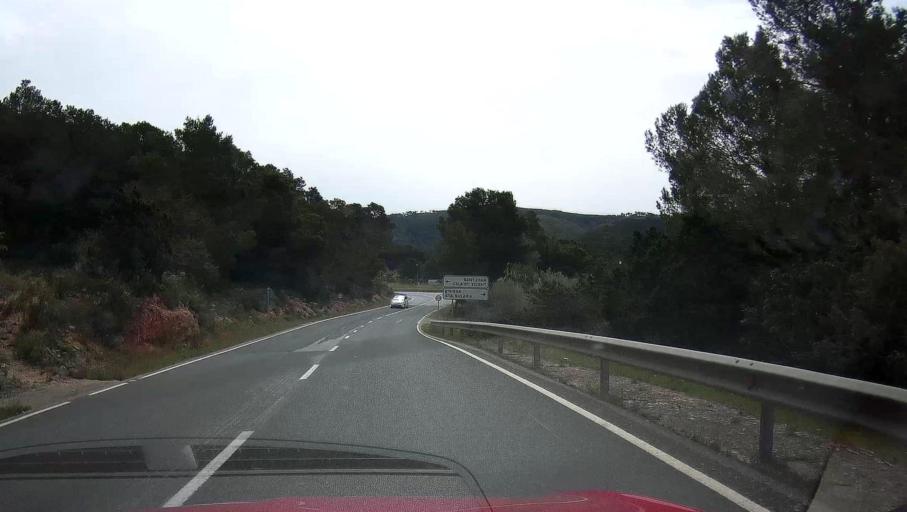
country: ES
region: Balearic Islands
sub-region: Illes Balears
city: Sant Joan de Labritja
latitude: 39.0767
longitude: 1.5034
